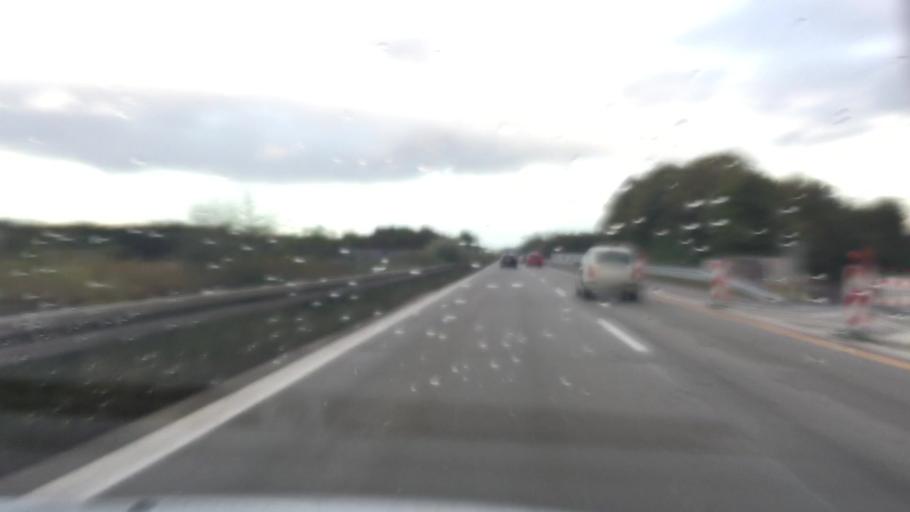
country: DE
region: Saxony-Anhalt
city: Diesdorf
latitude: 52.0606
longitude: 11.5847
